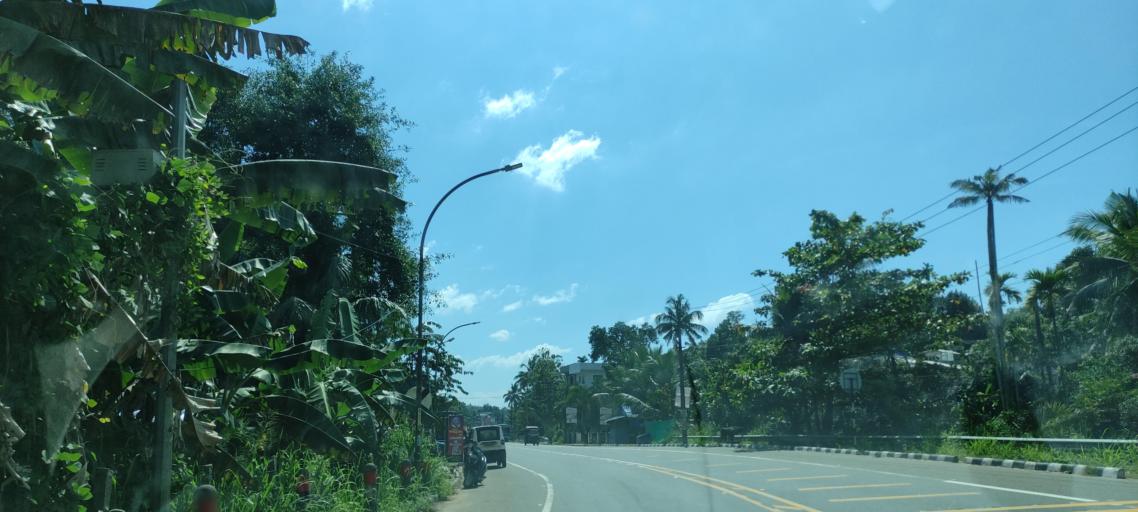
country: IN
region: Kerala
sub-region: Pattanamtitta
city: Adur
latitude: 9.1522
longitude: 76.7276
